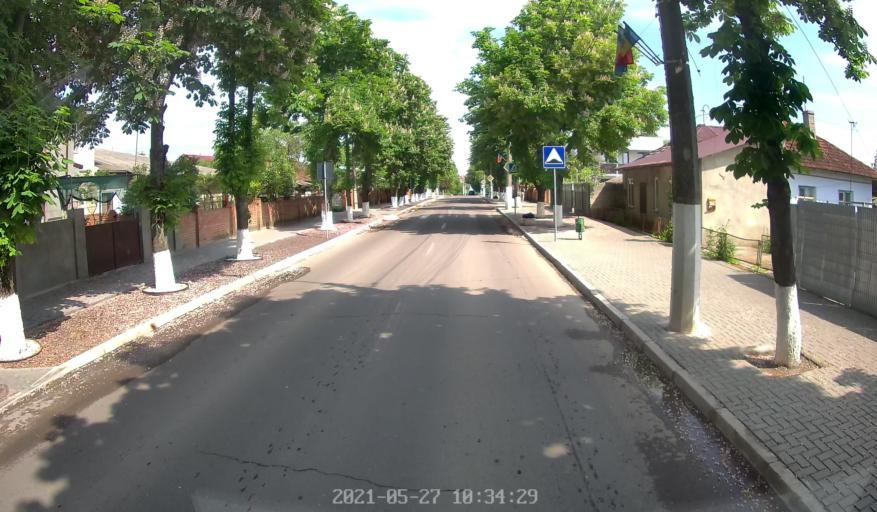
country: MD
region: Chisinau
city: Stauceni
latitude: 47.0899
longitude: 28.8682
